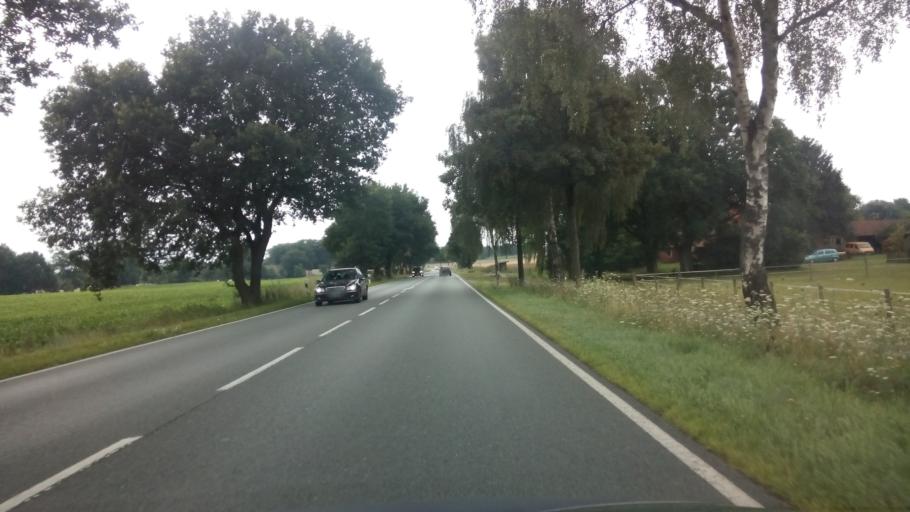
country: DE
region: Lower Saxony
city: Kirchseelte
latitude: 52.9396
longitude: 8.7089
